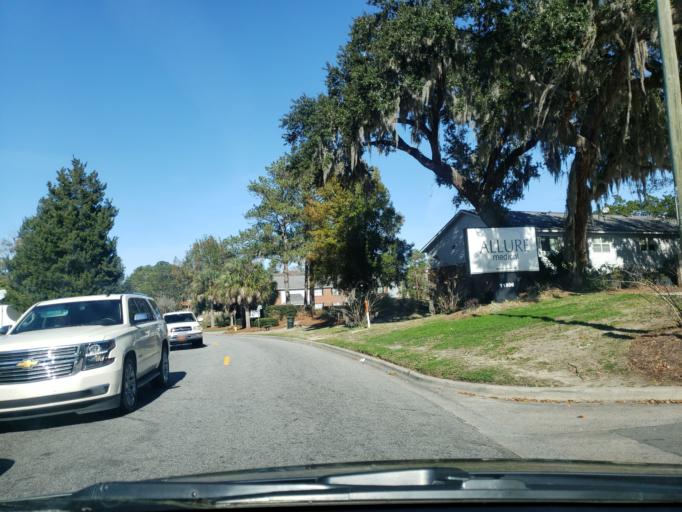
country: US
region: Georgia
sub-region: Chatham County
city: Montgomery
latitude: 31.9835
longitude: -81.1525
